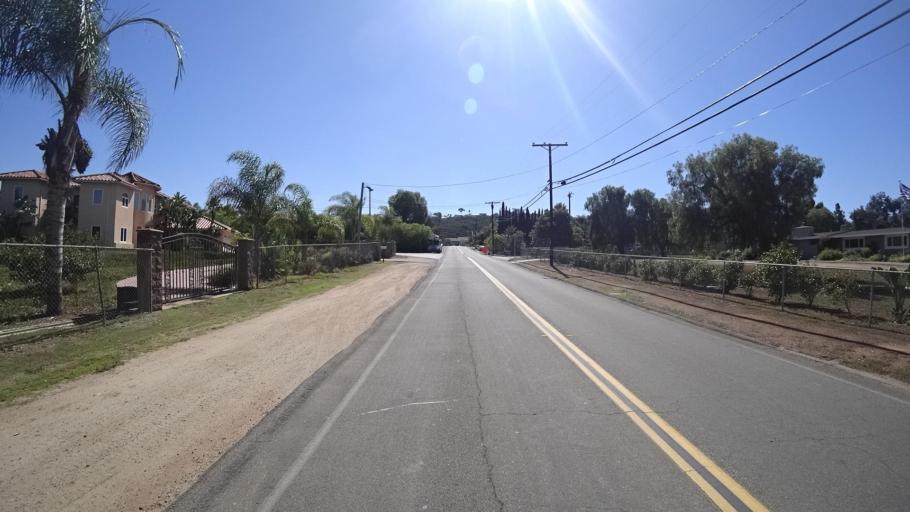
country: US
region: California
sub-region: San Diego County
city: Bonita
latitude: 32.6585
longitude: -117.0343
